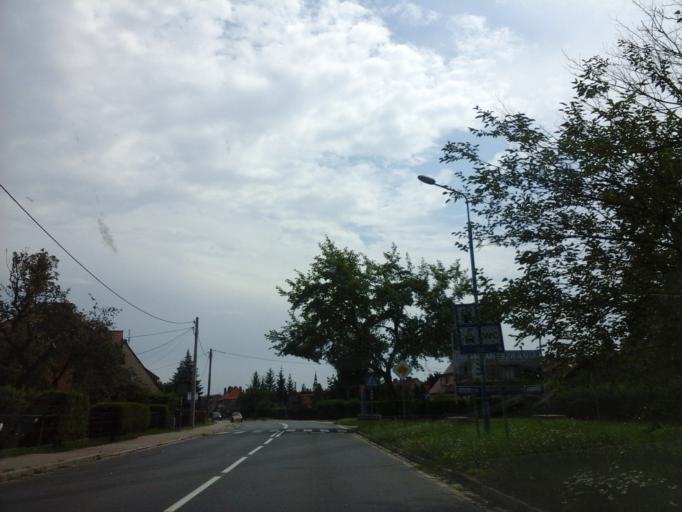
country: PL
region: Lower Silesian Voivodeship
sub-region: Powiat strzelinski
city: Strzelin
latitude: 50.7899
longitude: 17.0666
